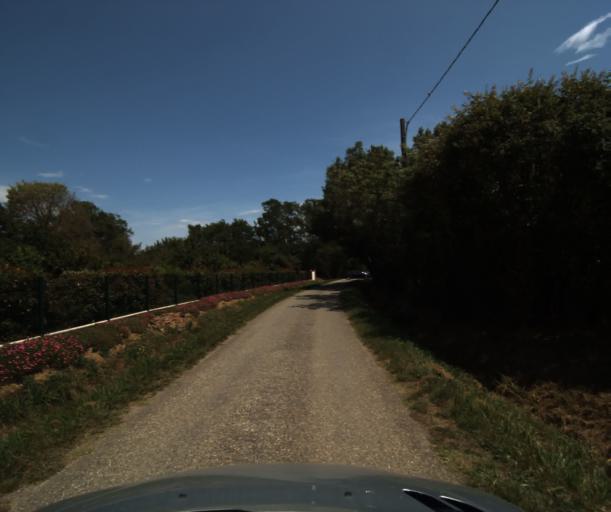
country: FR
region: Midi-Pyrenees
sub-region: Departement de la Haute-Garonne
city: Labastidette
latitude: 43.4629
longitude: 1.2354
